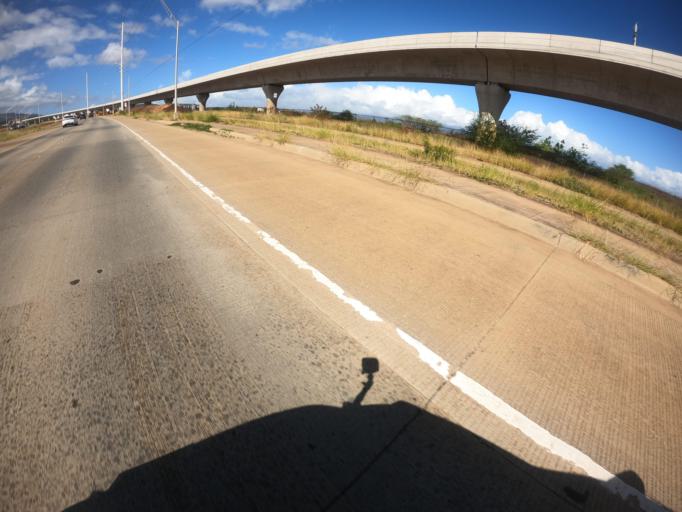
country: US
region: Hawaii
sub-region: Honolulu County
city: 'Ewa Villages
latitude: 21.3521
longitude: -158.0492
